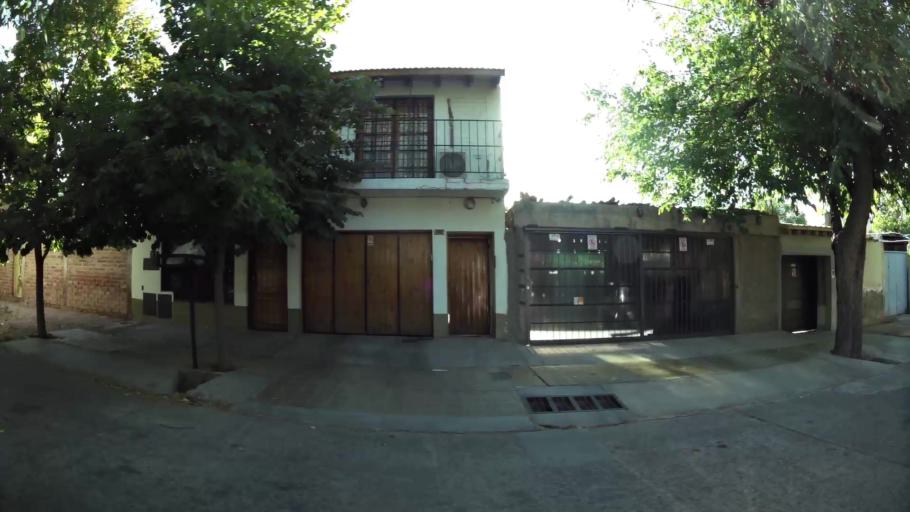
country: AR
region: Mendoza
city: Mendoza
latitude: -32.9060
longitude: -68.8414
